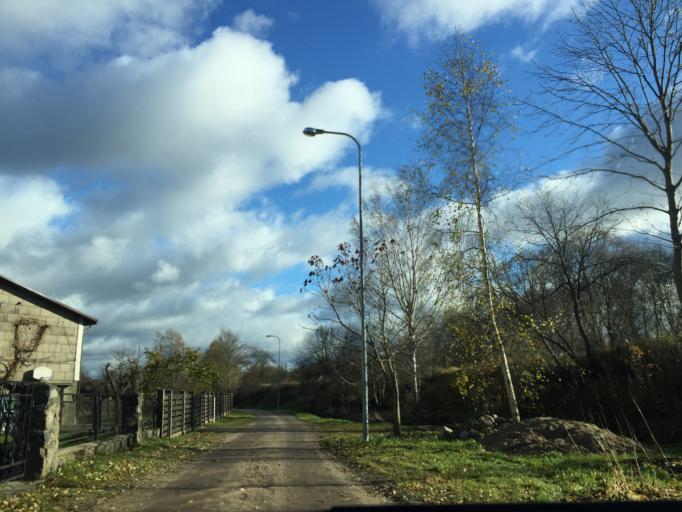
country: LV
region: Tukuma Rajons
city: Tukums
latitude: 56.9674
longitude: 23.1781
